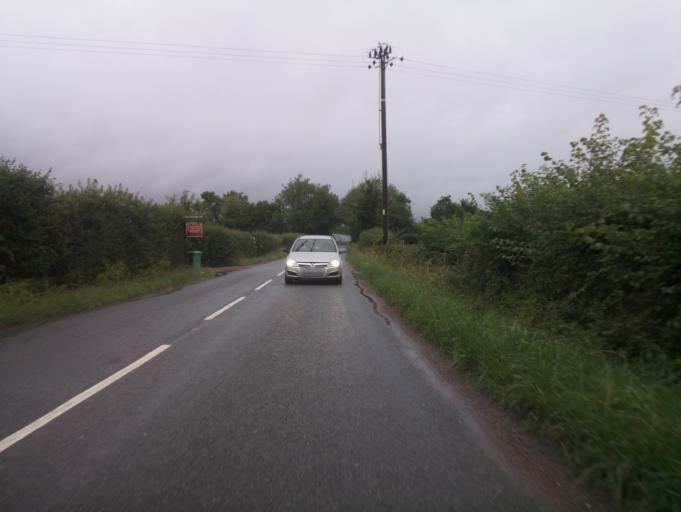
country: GB
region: England
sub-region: Gloucestershire
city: Uckington
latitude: 51.9535
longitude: -2.1244
